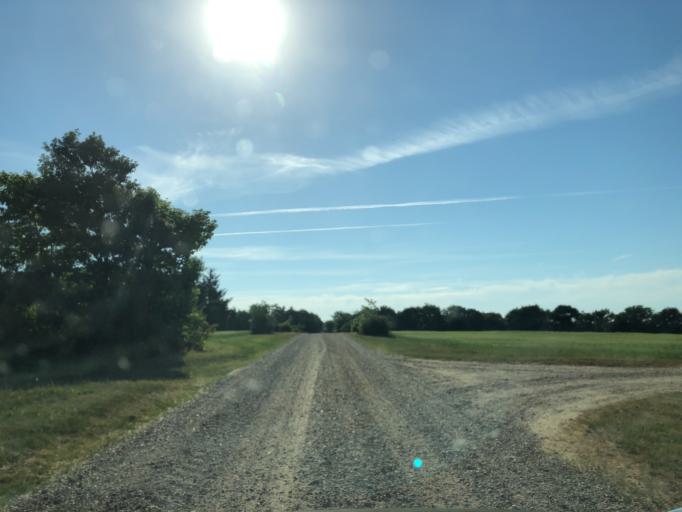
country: DK
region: Central Jutland
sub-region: Holstebro Kommune
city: Ulfborg
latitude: 56.3204
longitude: 8.3936
